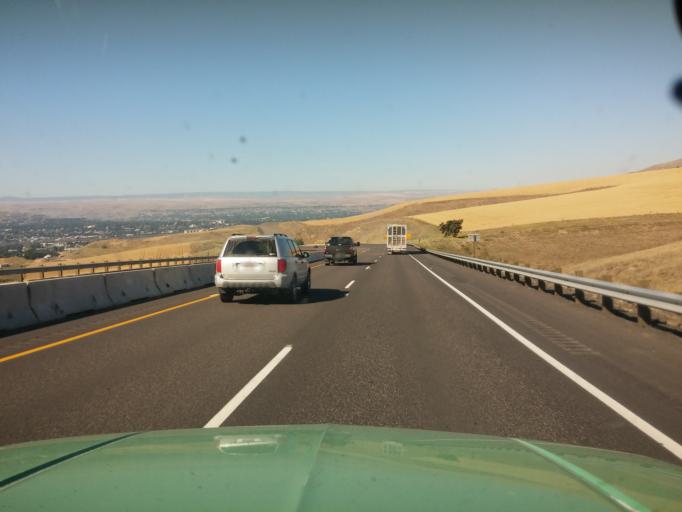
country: US
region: Idaho
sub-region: Nez Perce County
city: Lewiston
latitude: 46.4455
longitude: -116.9798
